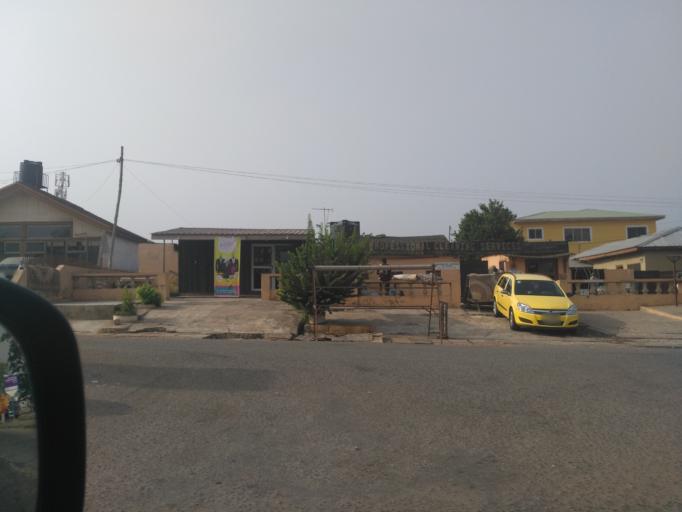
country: GH
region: Greater Accra
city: Accra
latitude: 5.5999
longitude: -0.1957
